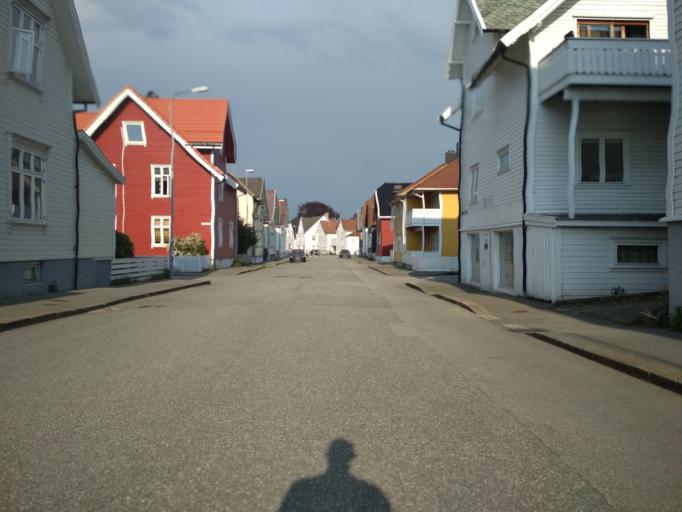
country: NO
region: Rogaland
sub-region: Stavanger
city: Stavanger
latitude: 58.9624
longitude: 5.7279
